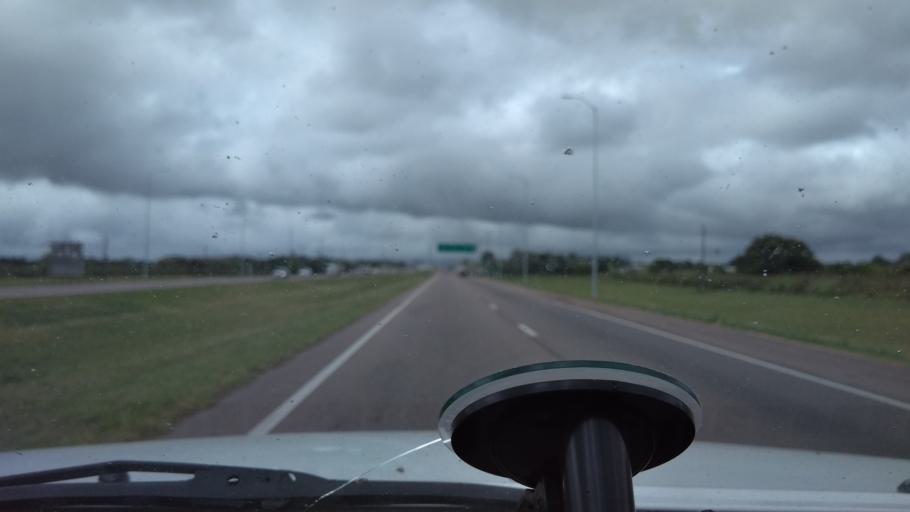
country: UY
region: Canelones
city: La Paz
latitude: -34.7779
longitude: -56.2729
